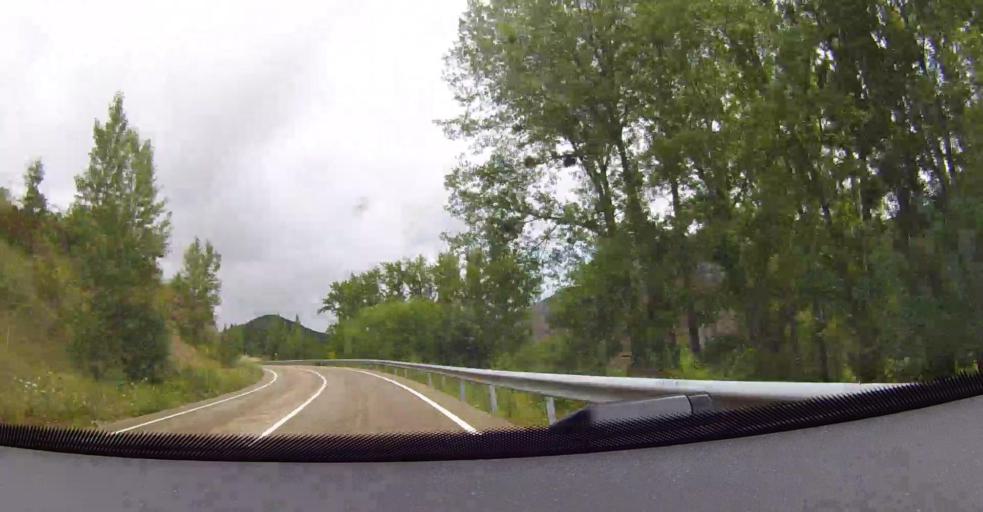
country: ES
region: Castille and Leon
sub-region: Provincia de Leon
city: Bonar
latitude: 42.9021
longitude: -5.3123
